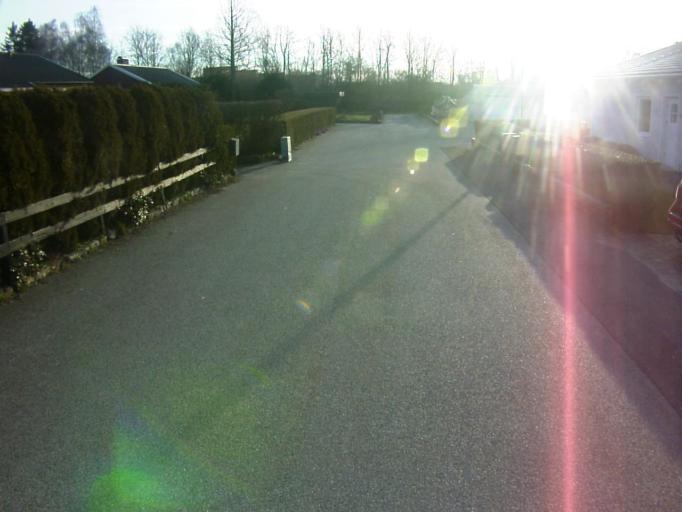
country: SE
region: Skane
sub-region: Kavlinge Kommun
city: Kaevlinge
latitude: 55.7953
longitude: 13.1284
